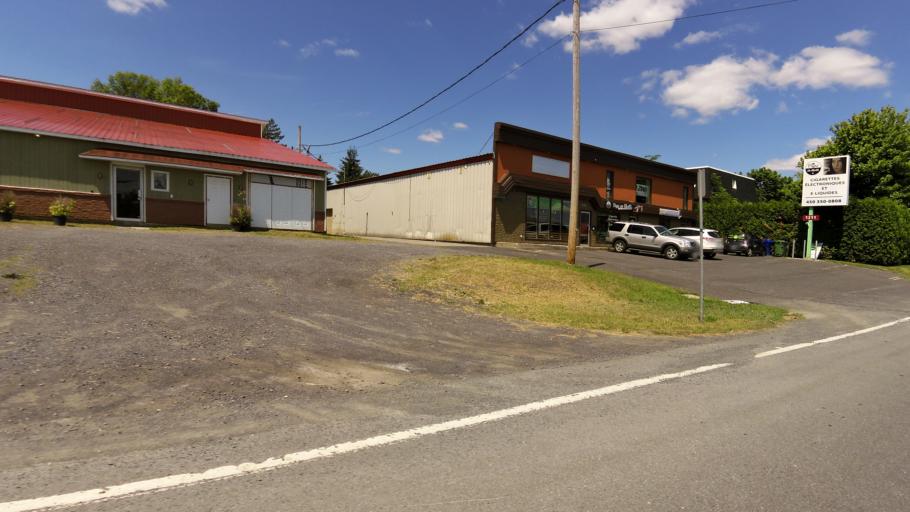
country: CA
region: Quebec
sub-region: Monteregie
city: Richelieu
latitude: 45.4389
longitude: -73.2457
